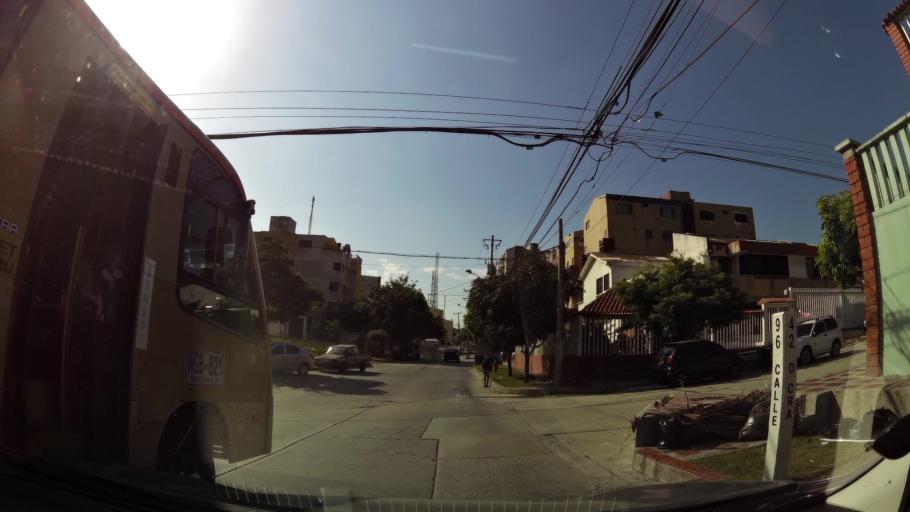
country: CO
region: Atlantico
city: Barranquilla
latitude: 10.9989
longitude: -74.8311
